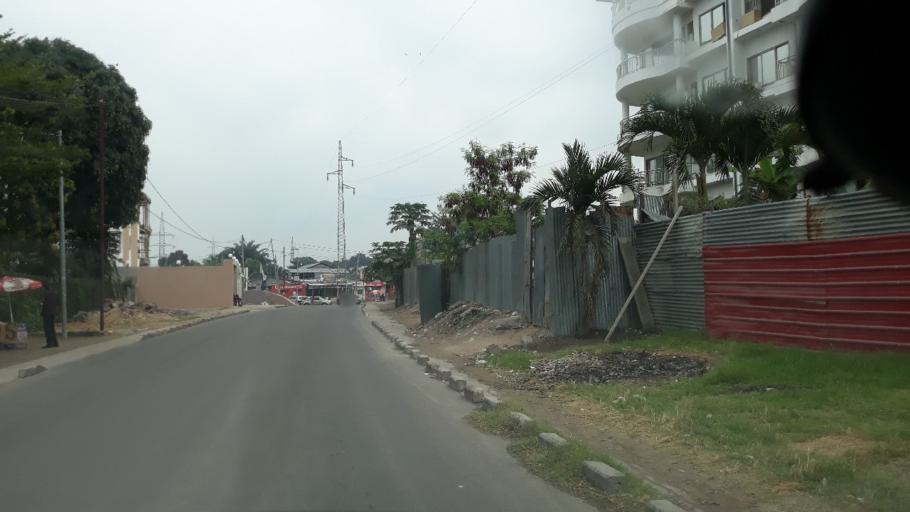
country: CD
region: Kinshasa
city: Kinshasa
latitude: -4.3221
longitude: 15.2782
